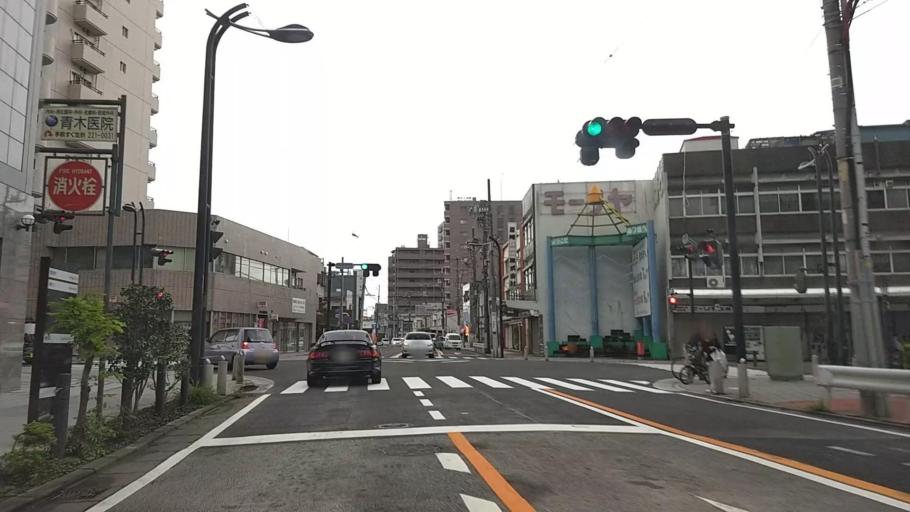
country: JP
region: Kanagawa
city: Atsugi
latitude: 35.4438
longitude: 139.3699
